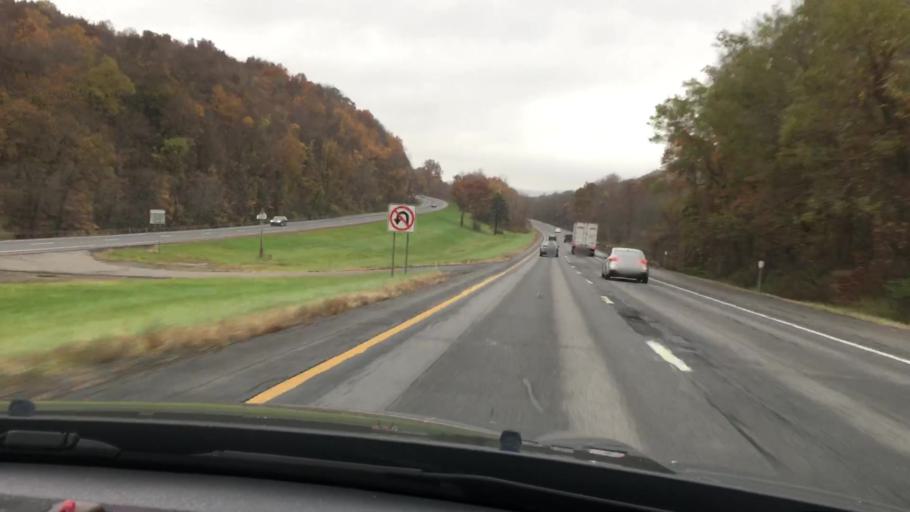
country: US
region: New York
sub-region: Putnam County
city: Lake Carmel
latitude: 41.4803
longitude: -73.6528
